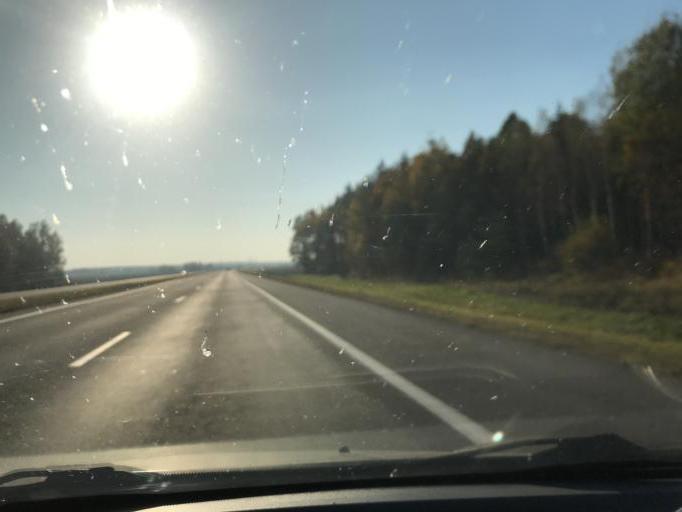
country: BY
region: Minsk
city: Hatava
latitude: 53.7500
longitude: 27.6420
